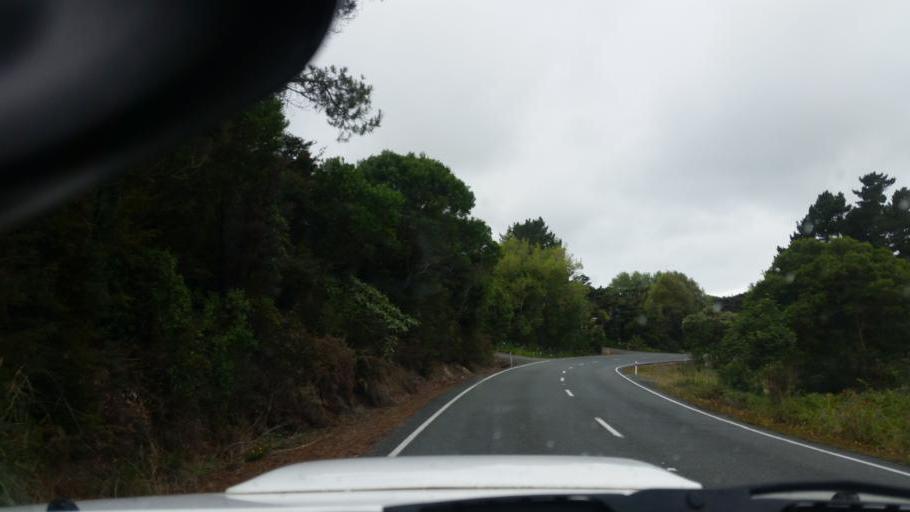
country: NZ
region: Auckland
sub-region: Auckland
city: Wellsford
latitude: -36.1312
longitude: 174.5511
